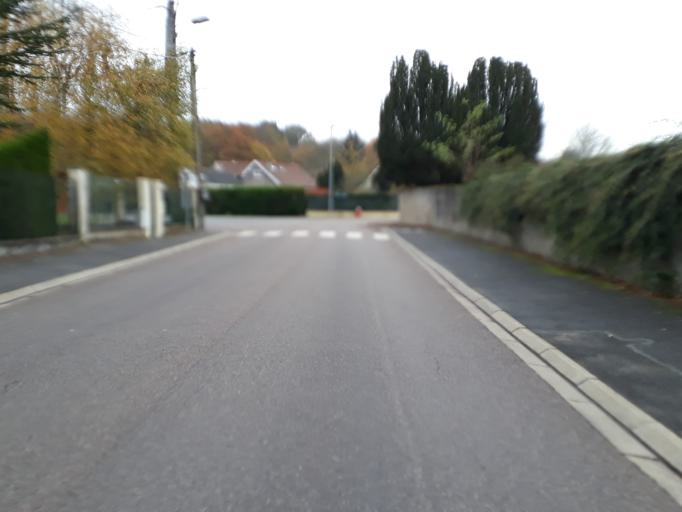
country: FR
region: Ile-de-France
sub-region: Departement de Seine-et-Marne
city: Bois-le-Roi
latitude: 48.4743
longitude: 2.7050
